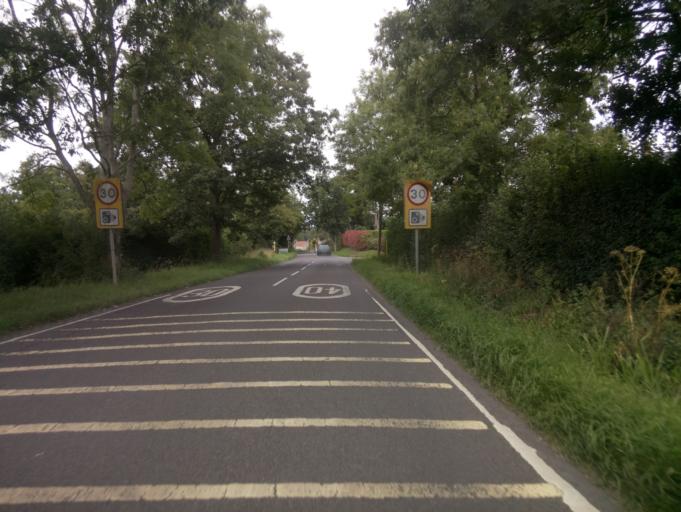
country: GB
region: England
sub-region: Somerset
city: Street
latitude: 51.0945
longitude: -2.6883
